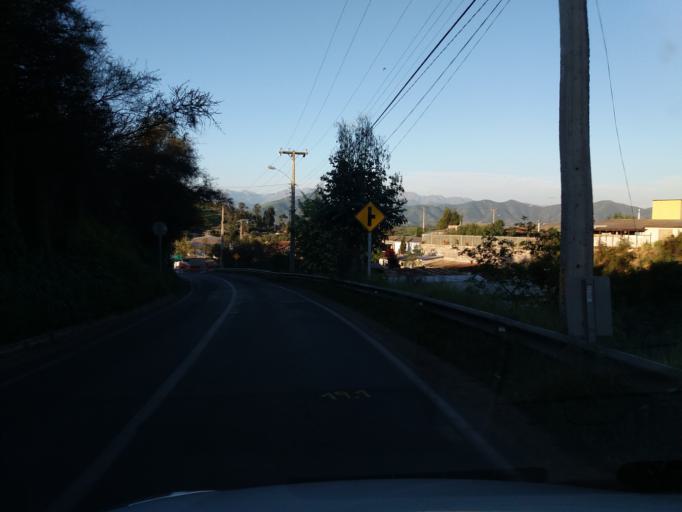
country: CL
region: Valparaiso
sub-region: Provincia de Quillota
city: Quillota
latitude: -32.8768
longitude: -71.2709
